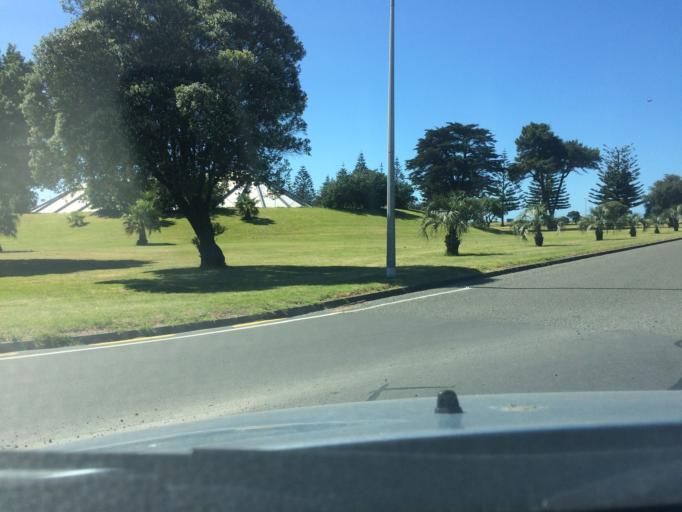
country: NZ
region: Gisborne
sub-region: Gisborne District
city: Gisborne
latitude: -38.6688
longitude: 178.0038
